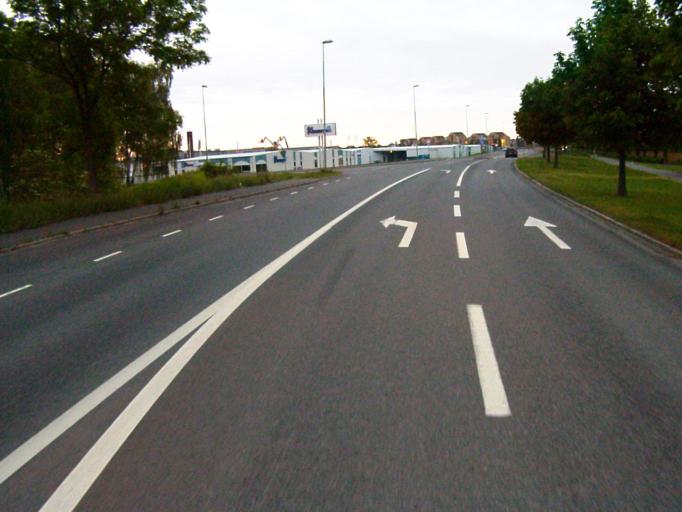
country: SE
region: Skane
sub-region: Kristianstads Kommun
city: Kristianstad
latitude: 56.0213
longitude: 14.1309
